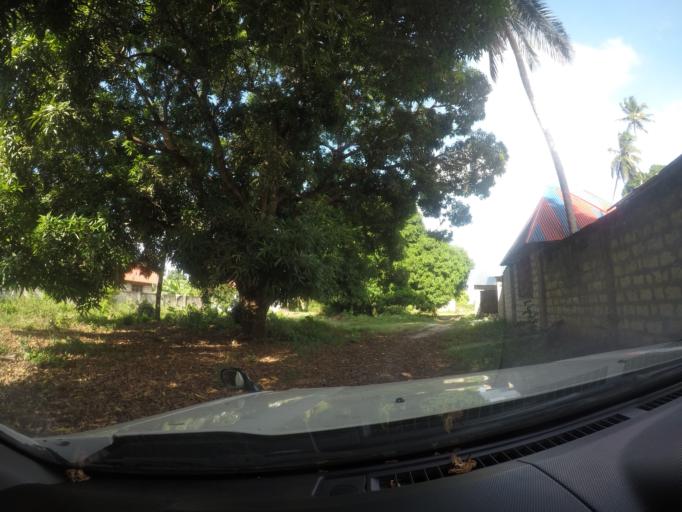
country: TZ
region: Pemba South
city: Chake Chake
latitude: -5.2488
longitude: 39.7855
